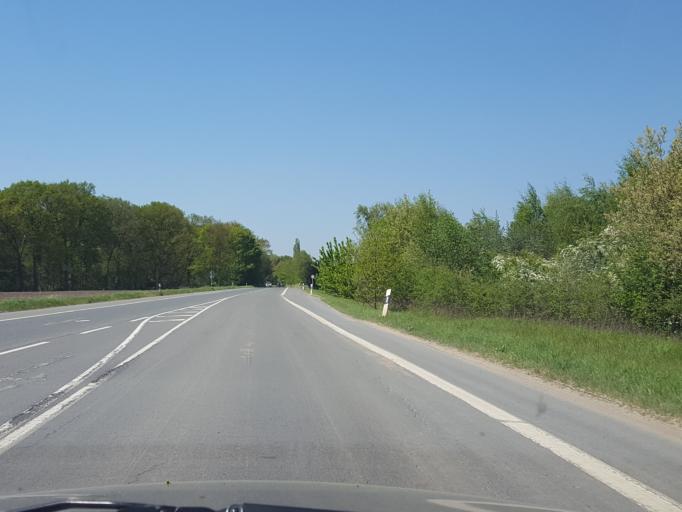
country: DE
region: North Rhine-Westphalia
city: Oer-Erkenschwick
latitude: 51.7112
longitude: 7.2845
